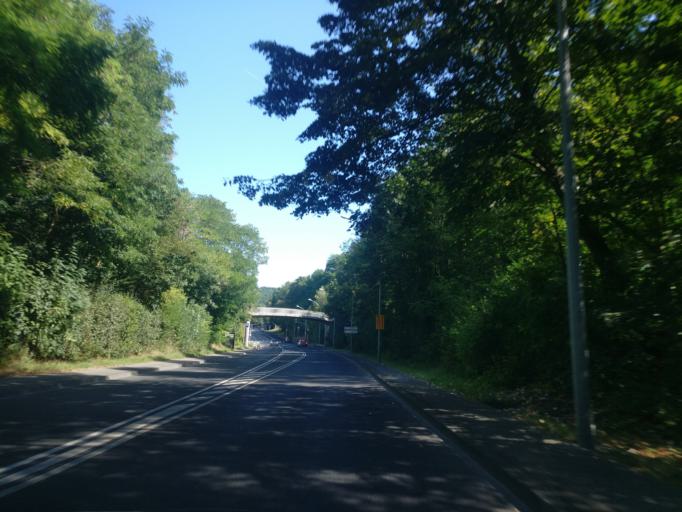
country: LU
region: Luxembourg
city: Kirchberg
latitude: 49.6333
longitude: 6.1401
